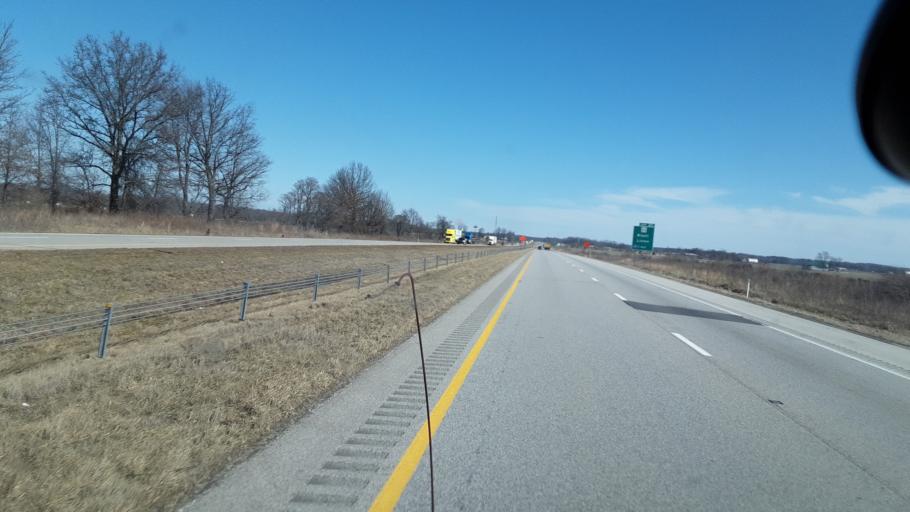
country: US
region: Indiana
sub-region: Clay County
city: Brazil
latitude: 39.4494
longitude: -87.1537
